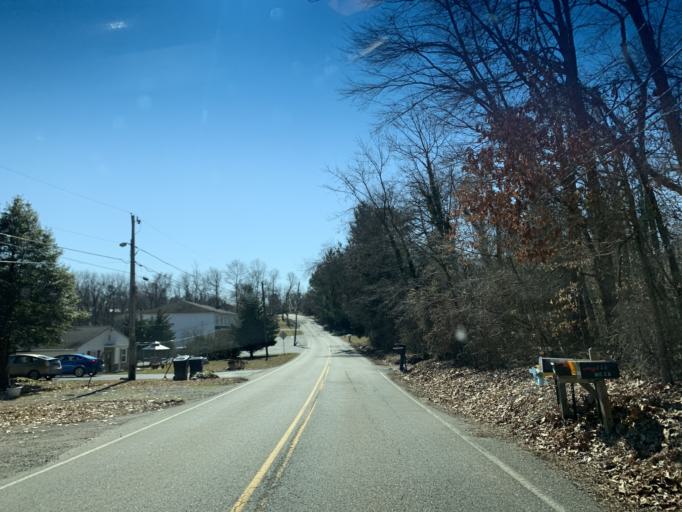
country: US
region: Maryland
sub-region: Cecil County
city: Perryville
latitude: 39.6059
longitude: -76.0731
